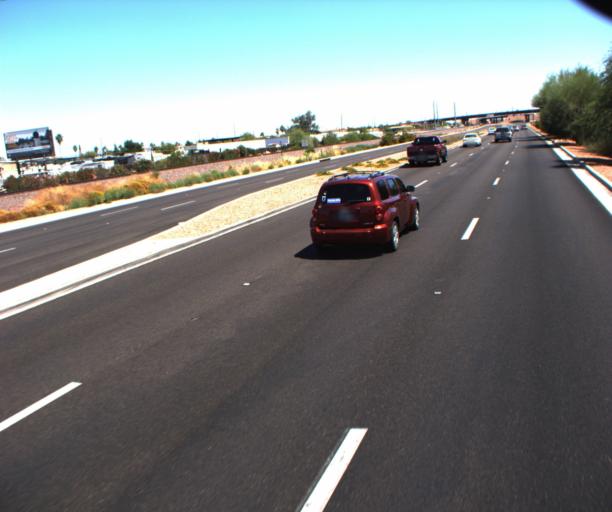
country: US
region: Arizona
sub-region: Maricopa County
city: Peoria
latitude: 33.5703
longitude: -112.2246
